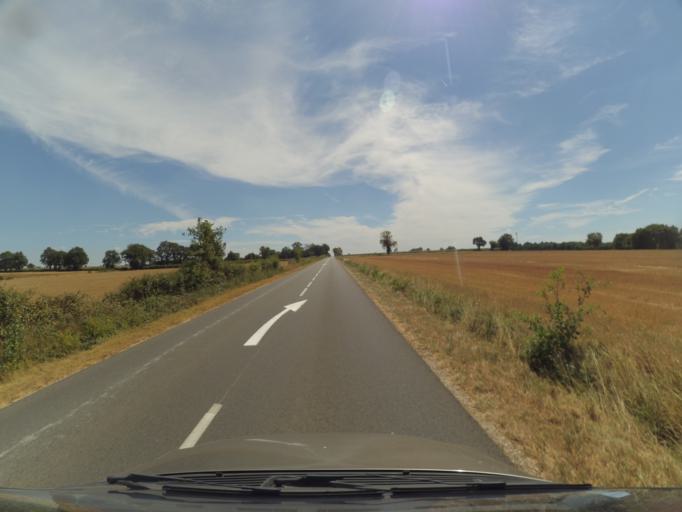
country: FR
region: Poitou-Charentes
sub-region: Departement de la Vienne
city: Availles-Limouzine
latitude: 46.1353
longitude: 0.5577
